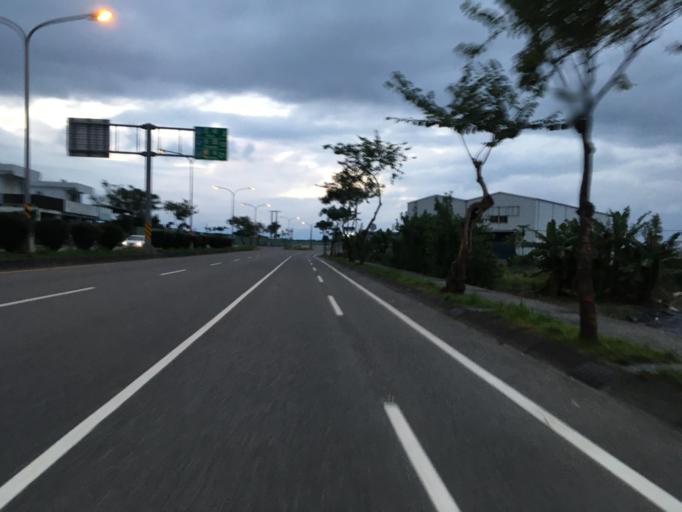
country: TW
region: Taiwan
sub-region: Yilan
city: Yilan
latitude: 24.6265
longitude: 121.8341
